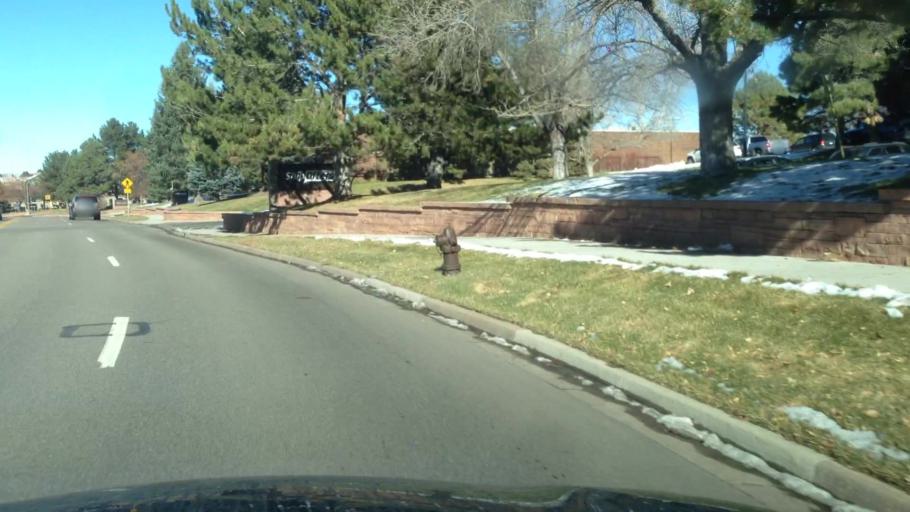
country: US
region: Colorado
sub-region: Douglas County
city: Meridian
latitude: 39.5723
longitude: -104.8563
